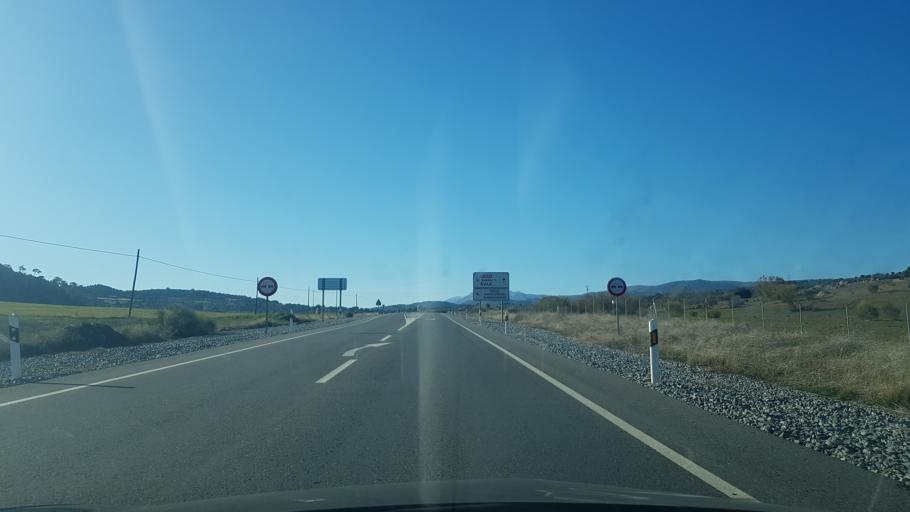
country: ES
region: Castille and Leon
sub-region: Provincia de Avila
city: Barraco
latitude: 40.4524
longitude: -4.5929
